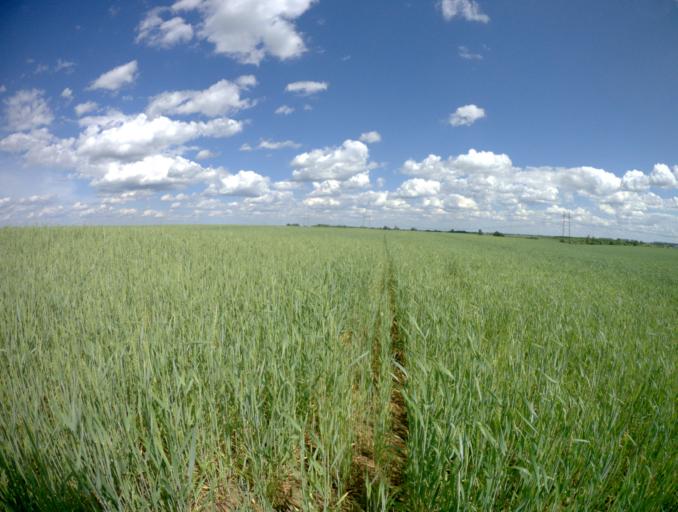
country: RU
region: Vladimir
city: Suzdal'
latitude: 56.4379
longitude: 40.3584
